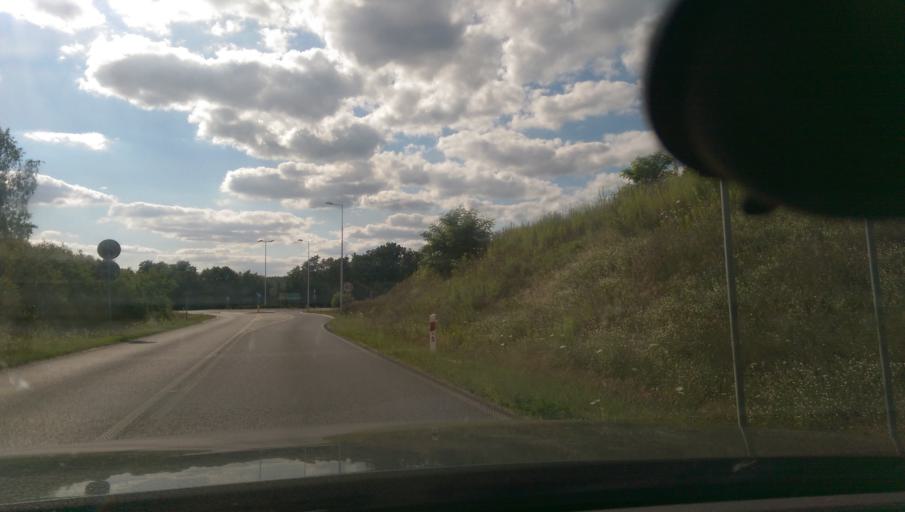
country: PL
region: Lubusz
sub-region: Powiat slubicki
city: Osno Lubuskie
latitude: 52.4606
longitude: 14.8854
